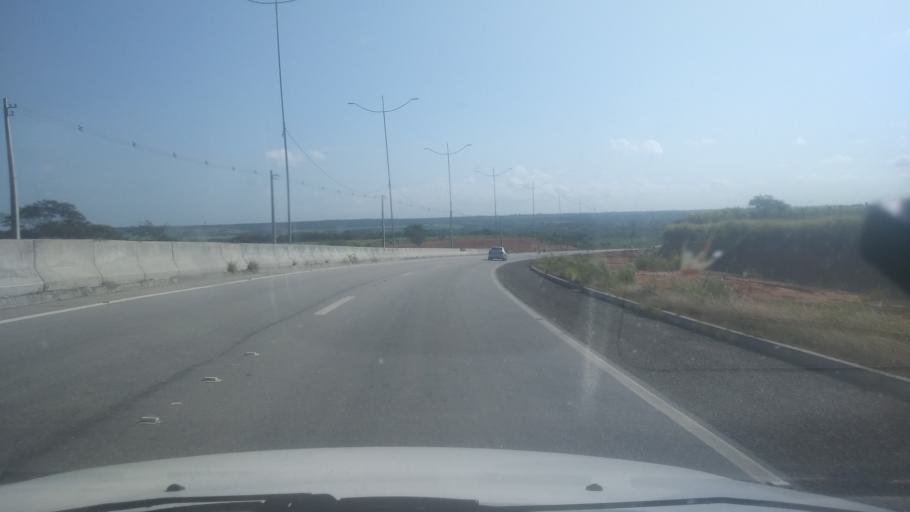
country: BR
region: Rio Grande do Norte
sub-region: Macaiba
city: Macaiba
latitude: -5.8253
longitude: -35.3698
